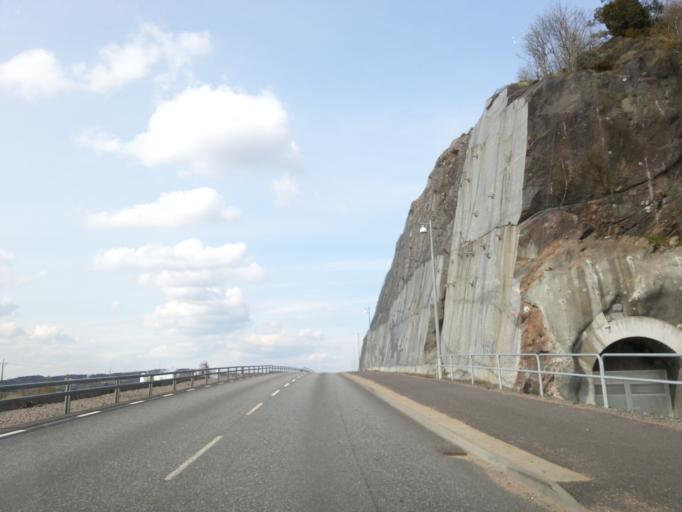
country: SE
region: Vaestra Goetaland
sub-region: Ale Kommun
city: Surte
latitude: 57.8413
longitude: 12.0138
